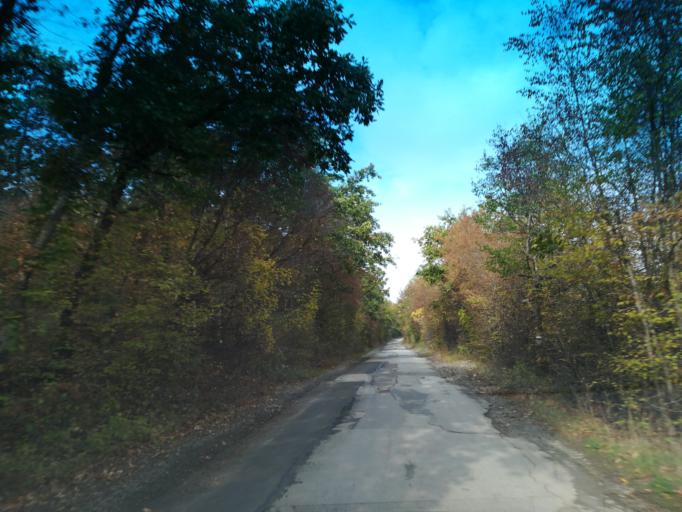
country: BG
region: Stara Zagora
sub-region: Obshtina Nikolaevo
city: Elkhovo
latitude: 42.3187
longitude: 25.4045
